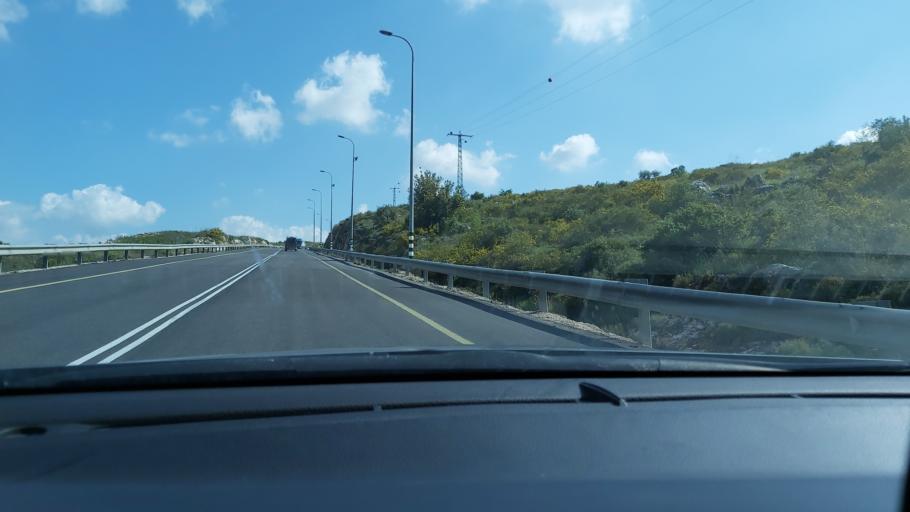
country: PS
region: West Bank
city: Bruqin
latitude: 32.0881
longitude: 35.1033
